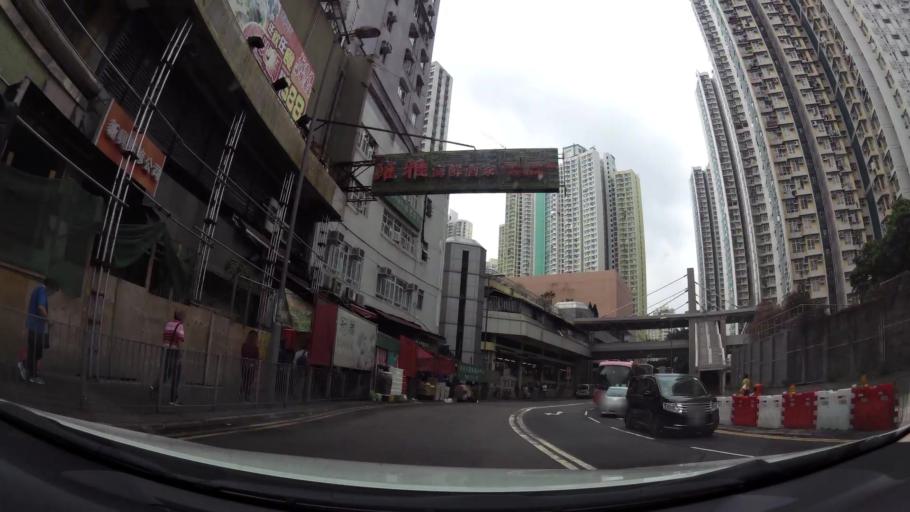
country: HK
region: Kowloon City
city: Kowloon
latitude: 22.3226
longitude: 114.2165
